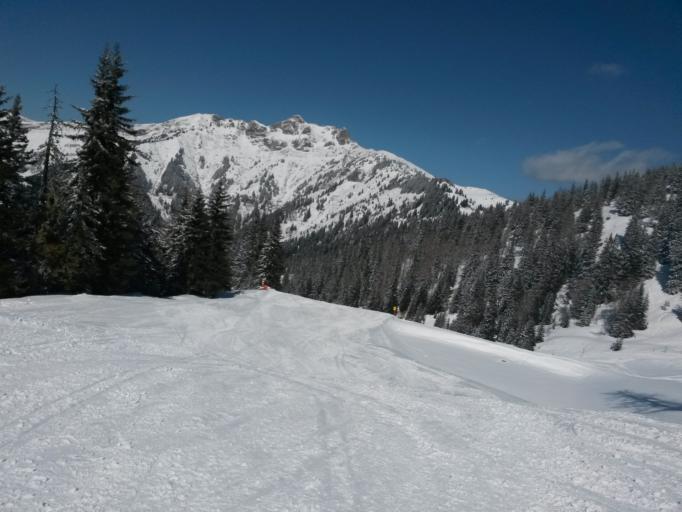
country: AT
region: Salzburg
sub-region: Politischer Bezirk Sankt Johann im Pongau
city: Dorfgastein
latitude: 47.2394
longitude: 13.1454
